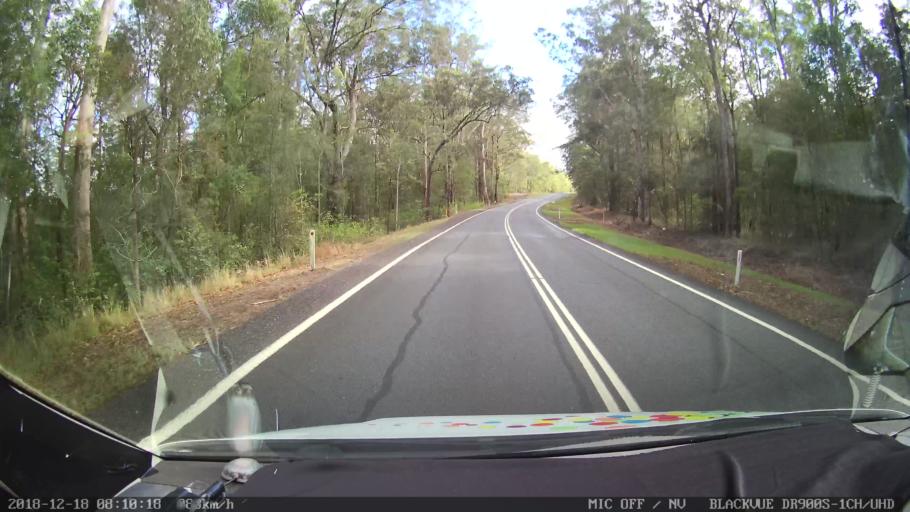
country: AU
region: New South Wales
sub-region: Kyogle
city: Kyogle
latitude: -28.3628
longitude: 152.6605
